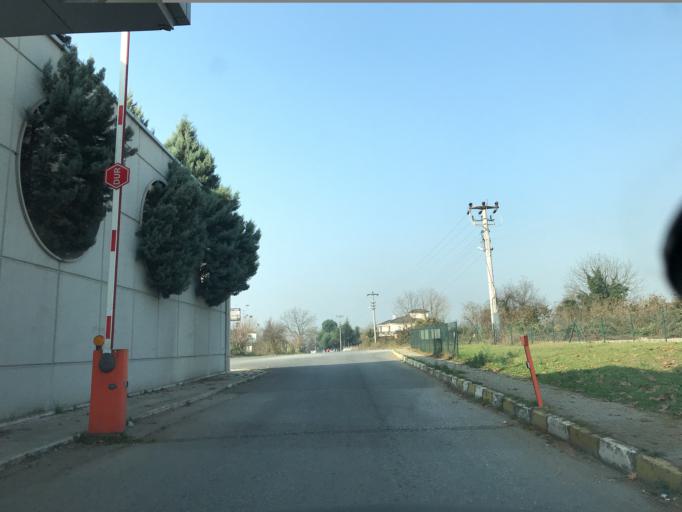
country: TR
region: Duzce
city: Duzce
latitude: 40.7893
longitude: 31.1311
